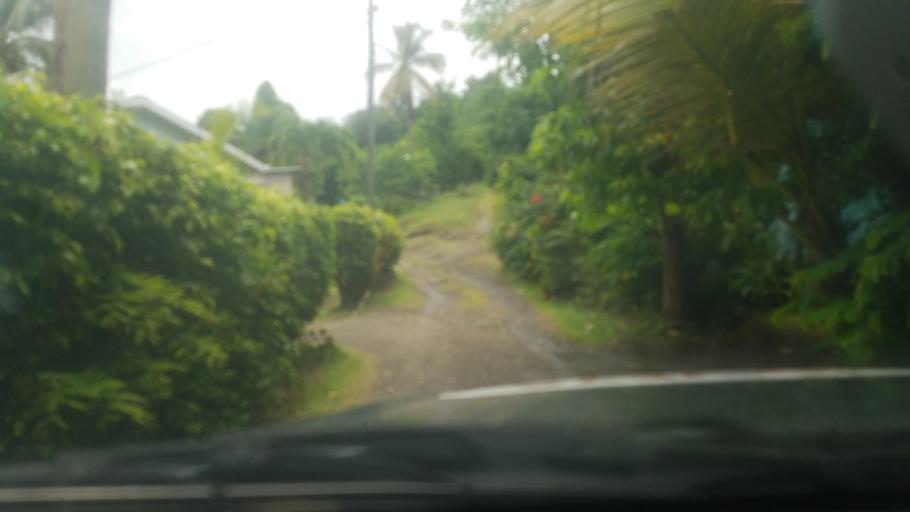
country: LC
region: Gros-Islet
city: Gros Islet
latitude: 14.0500
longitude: -60.9374
